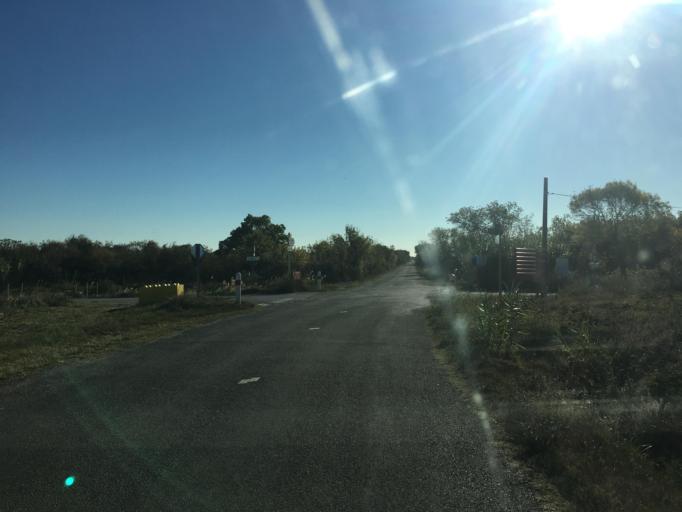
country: FR
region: Languedoc-Roussillon
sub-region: Departement de l'Herault
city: Lespignan
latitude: 43.2332
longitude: 3.1927
